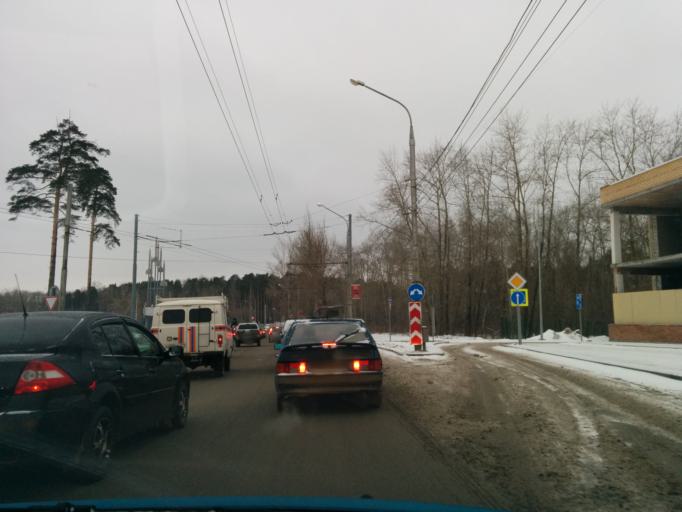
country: RU
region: Perm
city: Perm
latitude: 57.9904
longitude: 56.1926
